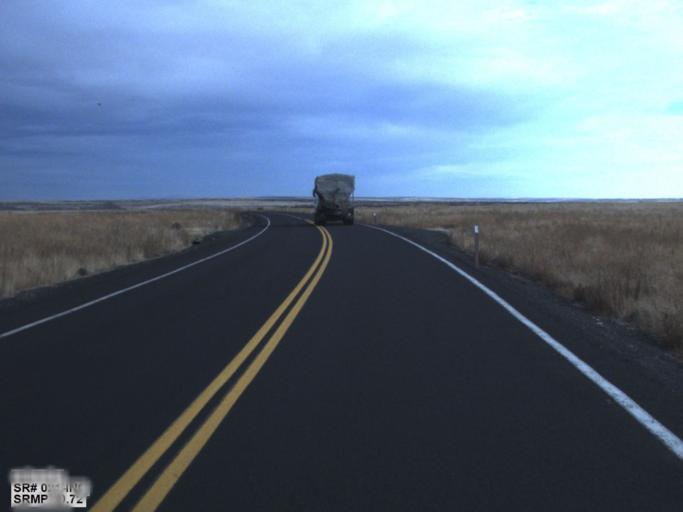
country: US
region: Washington
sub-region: Adams County
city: Ritzville
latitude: 47.3968
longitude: -118.6868
